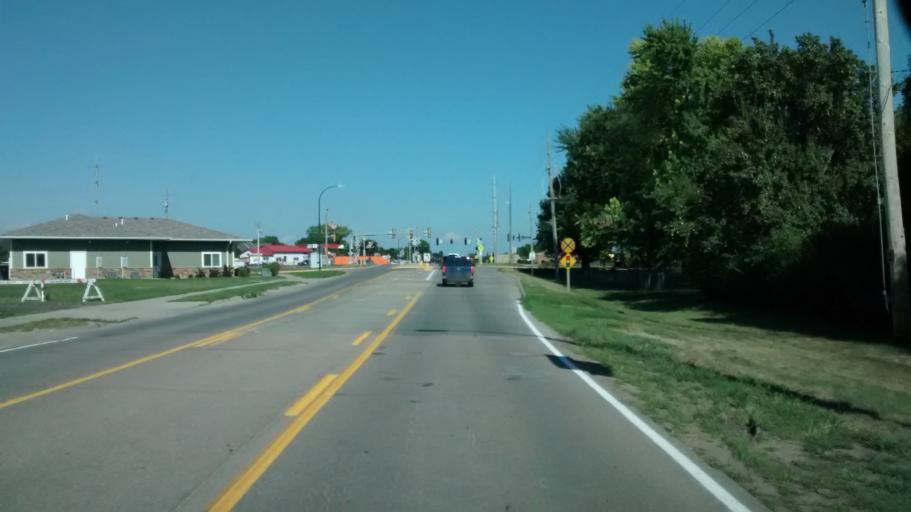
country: US
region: Iowa
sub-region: Woodbury County
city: Sergeant Bluff
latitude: 42.4004
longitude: -96.3570
